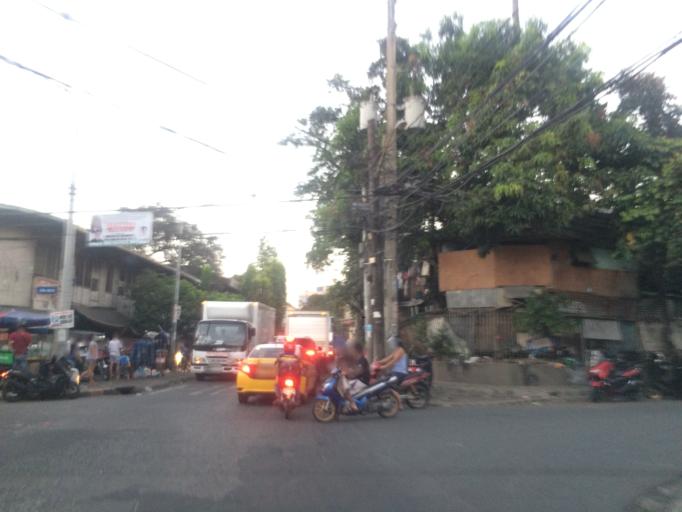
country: PH
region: Calabarzon
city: Del Monte
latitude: 14.6417
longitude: 121.0133
